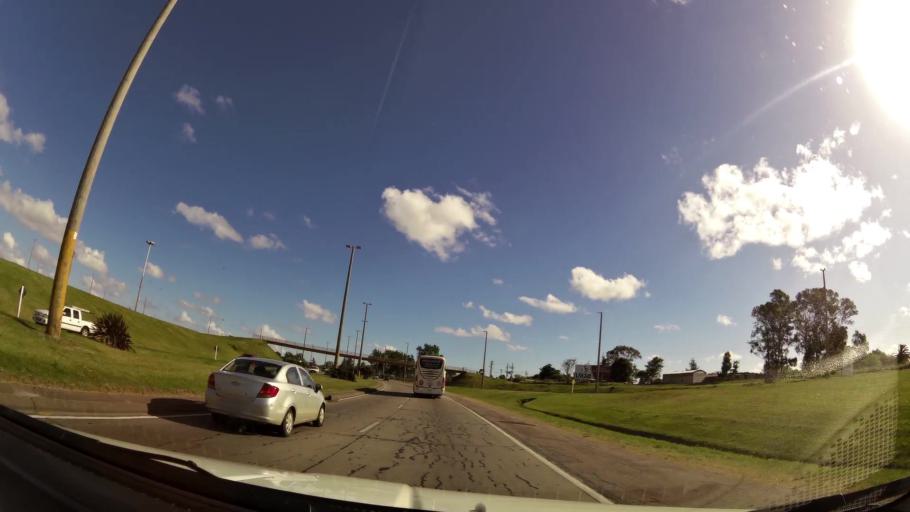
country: UY
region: Montevideo
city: Montevideo
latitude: -34.8580
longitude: -56.2568
